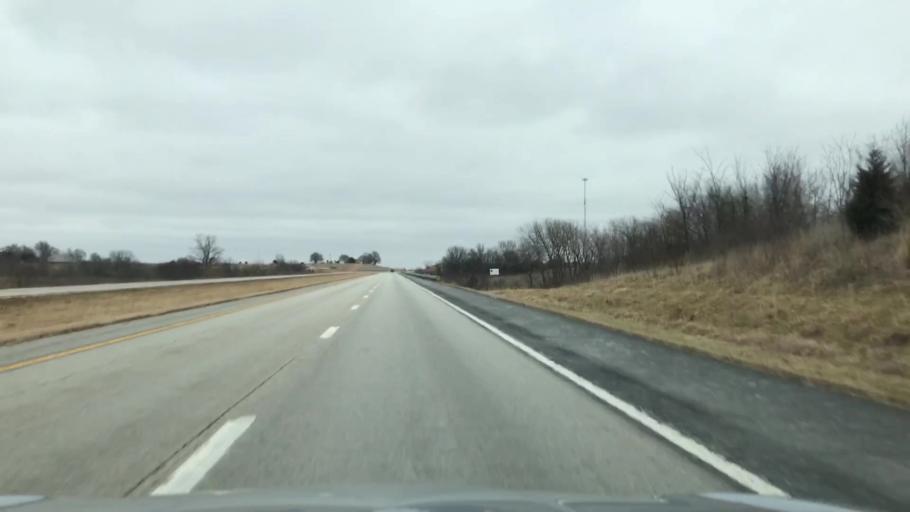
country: US
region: Missouri
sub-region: Caldwell County
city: Hamilton
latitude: 39.7490
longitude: -94.0635
